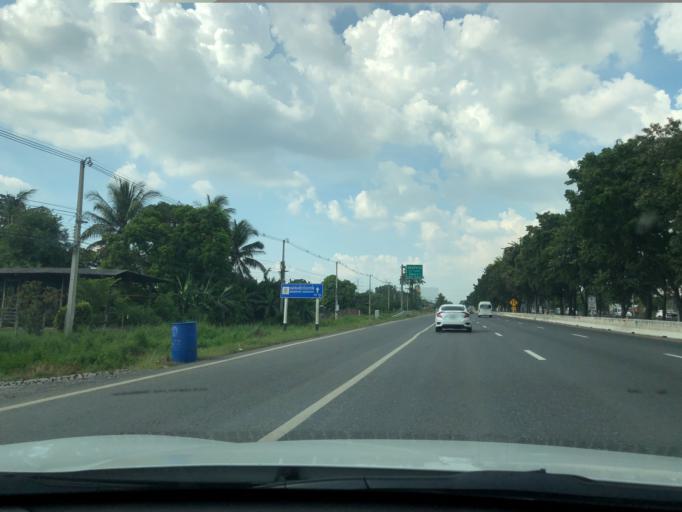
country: TH
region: Nakhon Sawan
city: Krok Phra
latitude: 15.5847
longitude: 100.1240
